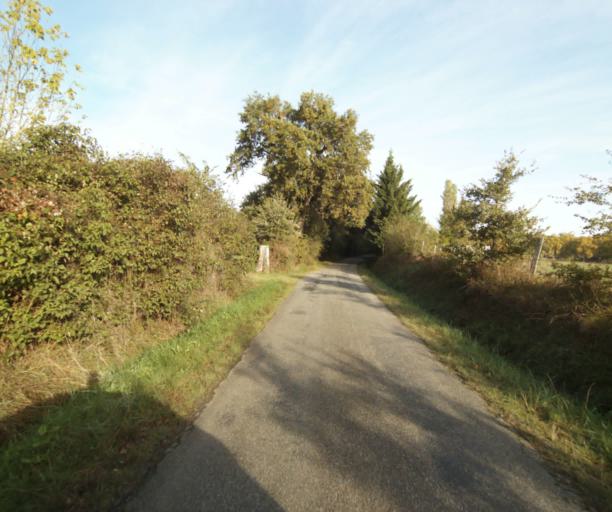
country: FR
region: Midi-Pyrenees
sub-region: Departement de la Haute-Garonne
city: Villemur-sur-Tarn
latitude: 43.9251
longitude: 1.5049
